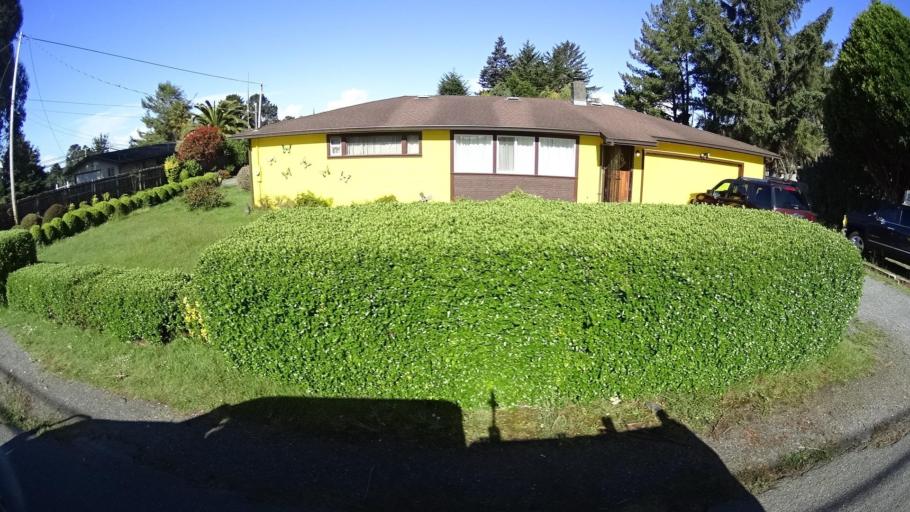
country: US
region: California
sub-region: Humboldt County
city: McKinleyville
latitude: 40.9640
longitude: -124.0960
